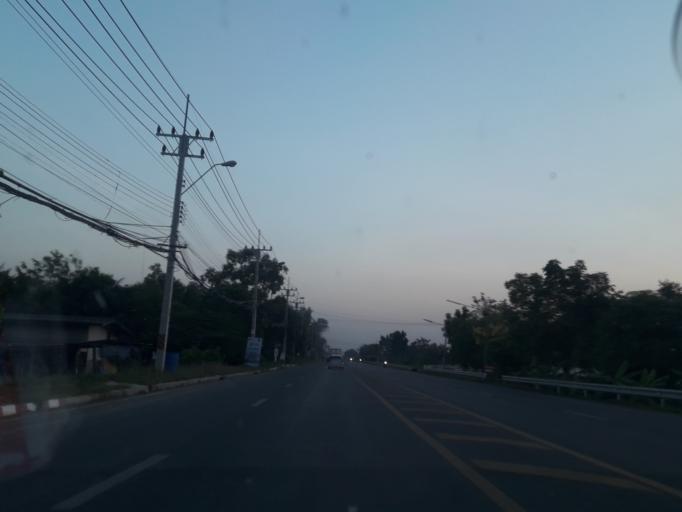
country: TH
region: Pathum Thani
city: Thanyaburi
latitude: 14.0833
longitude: 100.7103
